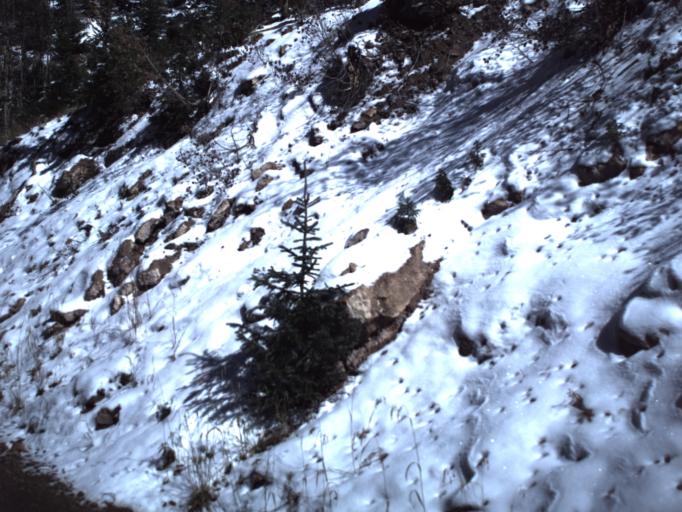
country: US
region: Utah
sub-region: Piute County
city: Junction
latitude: 38.3053
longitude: -112.3643
